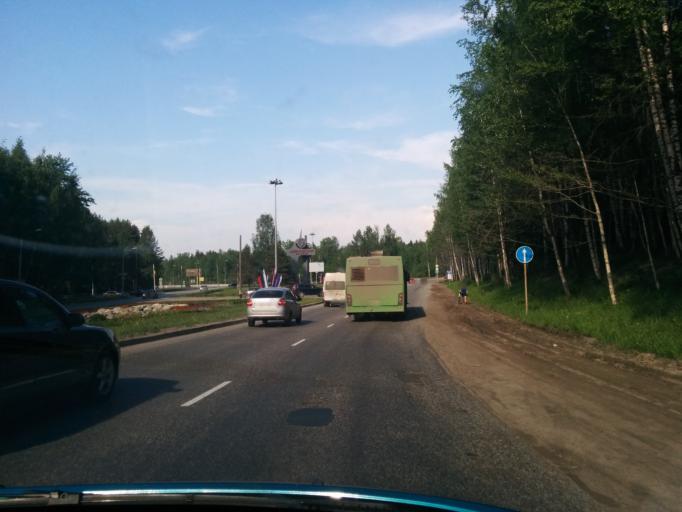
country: RU
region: Perm
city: Kondratovo
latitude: 58.0446
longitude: 56.0582
